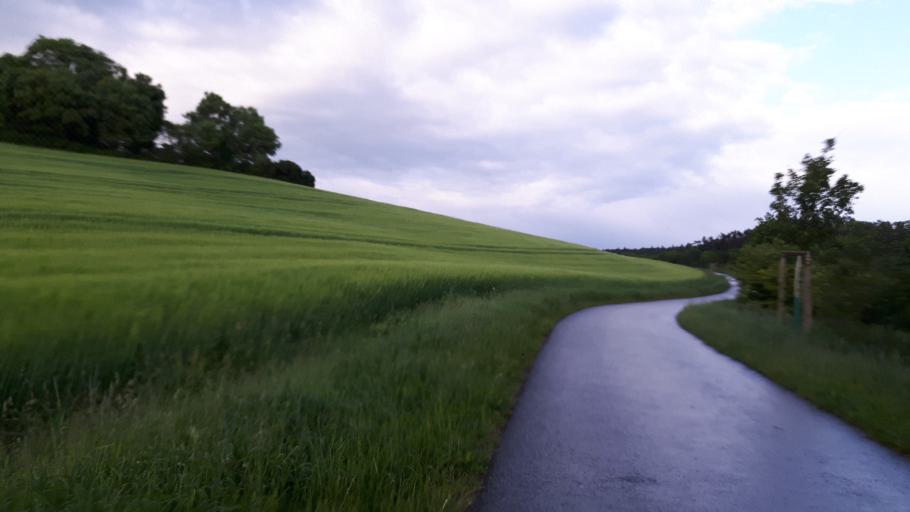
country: DE
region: Thuringia
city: Hetschburg
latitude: 50.9137
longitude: 11.3054
